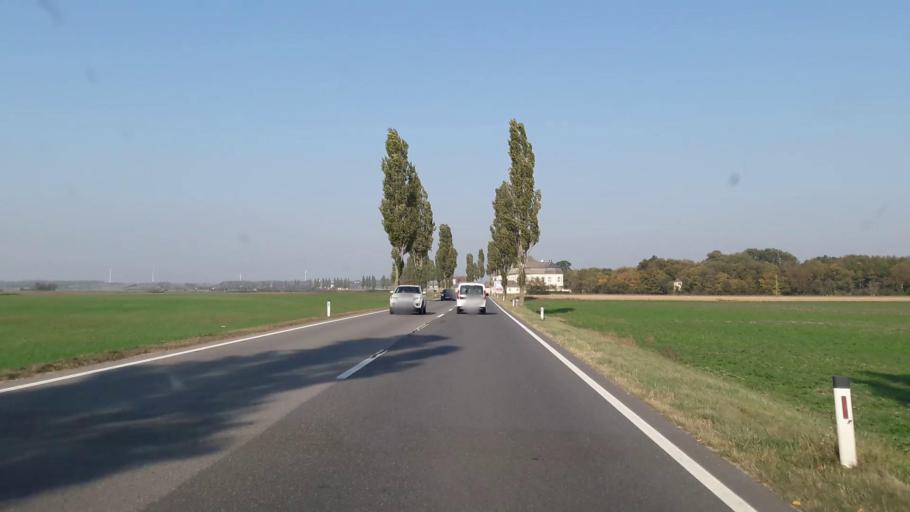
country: AT
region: Lower Austria
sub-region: Politischer Bezirk Ganserndorf
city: Engelhartstetten
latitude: 48.1940
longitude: 16.8987
